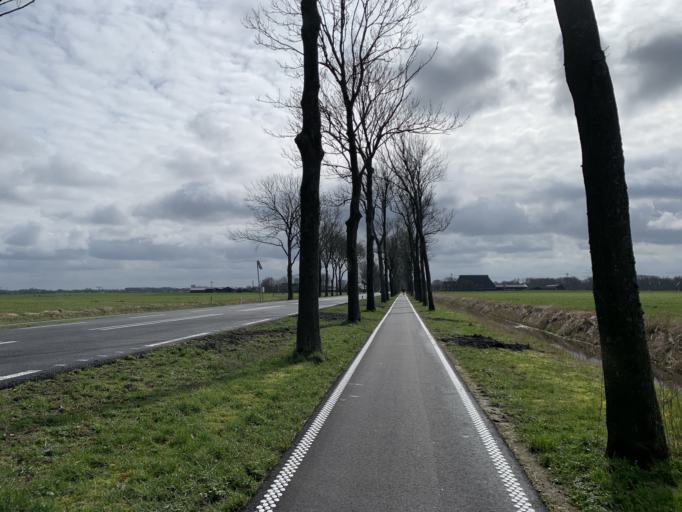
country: NL
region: Groningen
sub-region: Gemeente Groningen
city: Korrewegwijk
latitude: 53.2567
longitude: 6.5409
